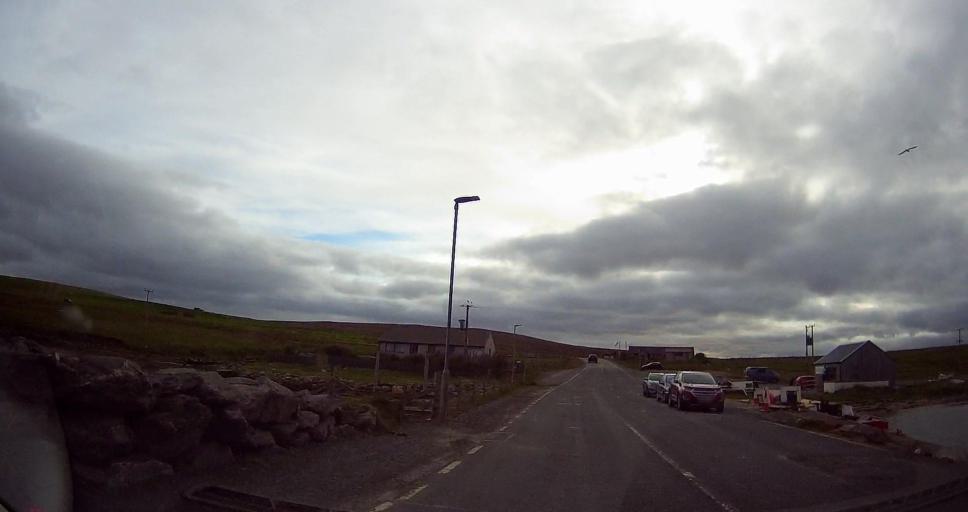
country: GB
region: Scotland
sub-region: Shetland Islands
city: Lerwick
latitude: 60.4667
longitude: -1.2076
